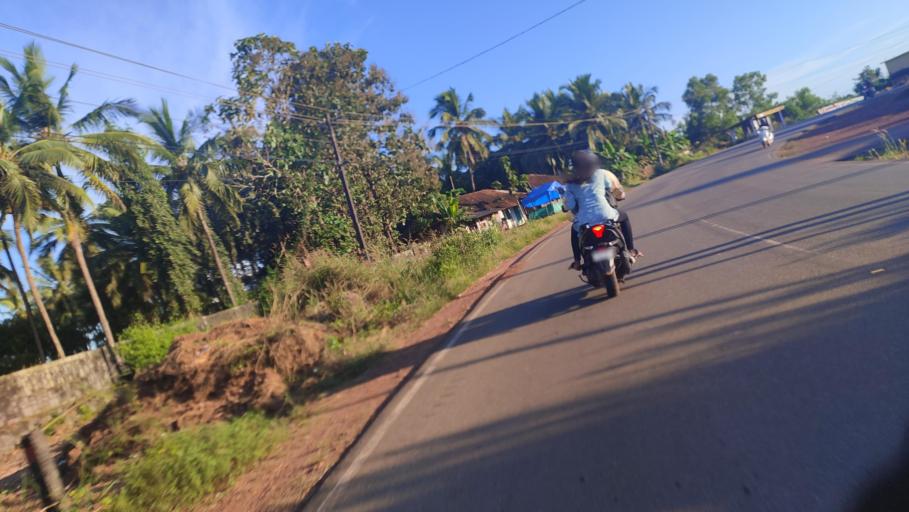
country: IN
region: Kerala
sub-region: Kasaragod District
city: Kasaragod
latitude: 12.4743
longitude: 75.0595
